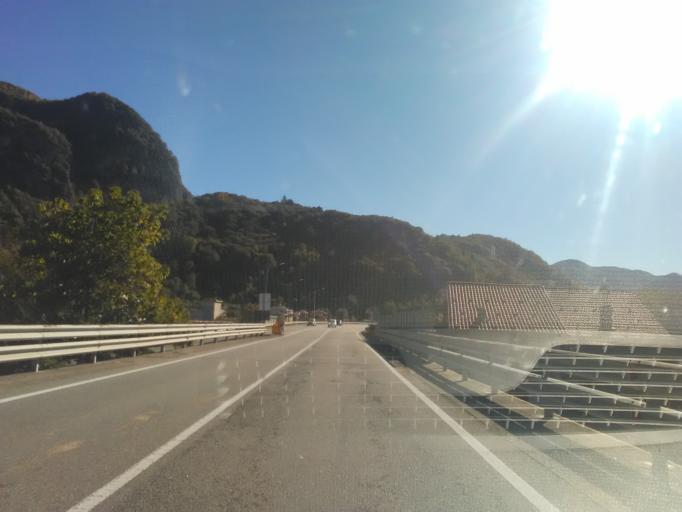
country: IT
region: Piedmont
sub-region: Provincia di Vercelli
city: Varallo
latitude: 45.8094
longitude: 8.2622
